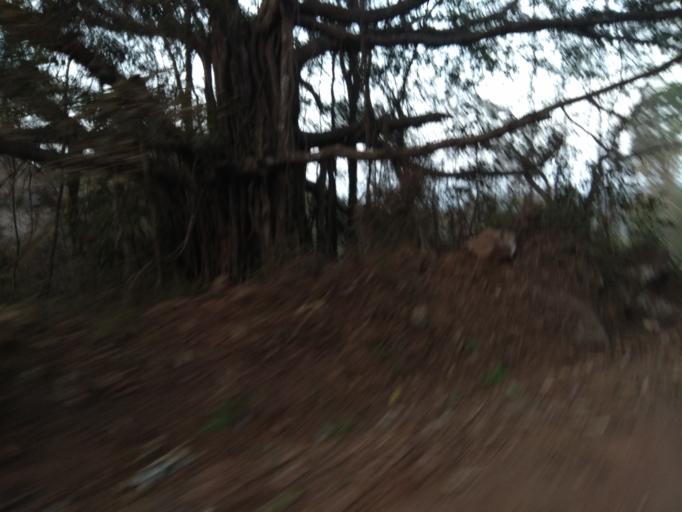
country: IN
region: Karnataka
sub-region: Dakshina Kannada
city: Mangalore
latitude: 12.9276
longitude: 74.8753
